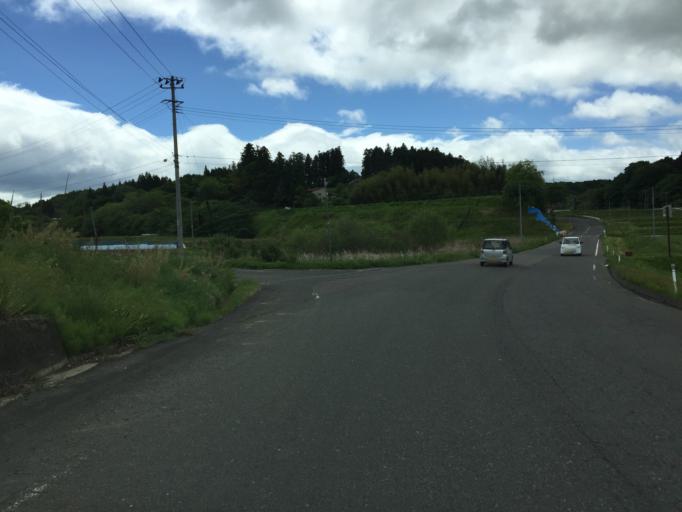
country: JP
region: Fukushima
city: Miharu
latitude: 37.4822
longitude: 140.4679
